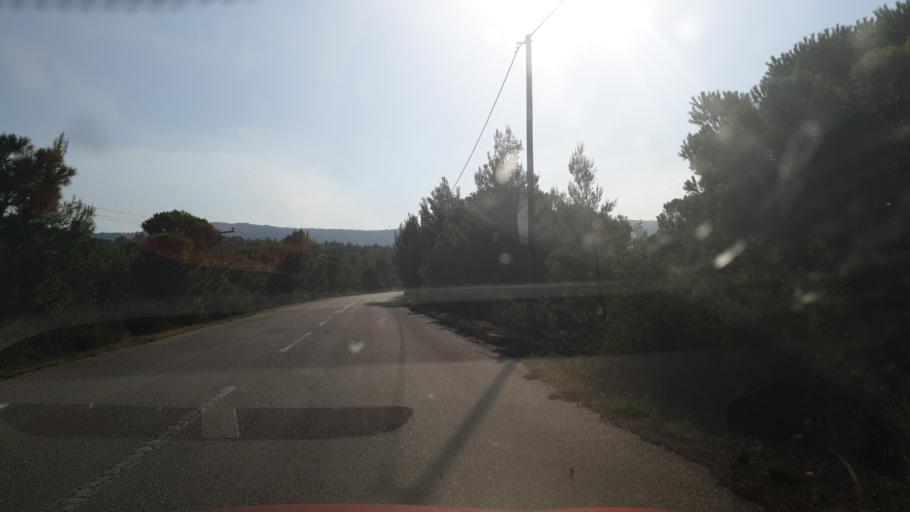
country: GR
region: Central Macedonia
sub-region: Nomos Chalkidikis
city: Sarti
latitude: 40.1254
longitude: 23.9584
